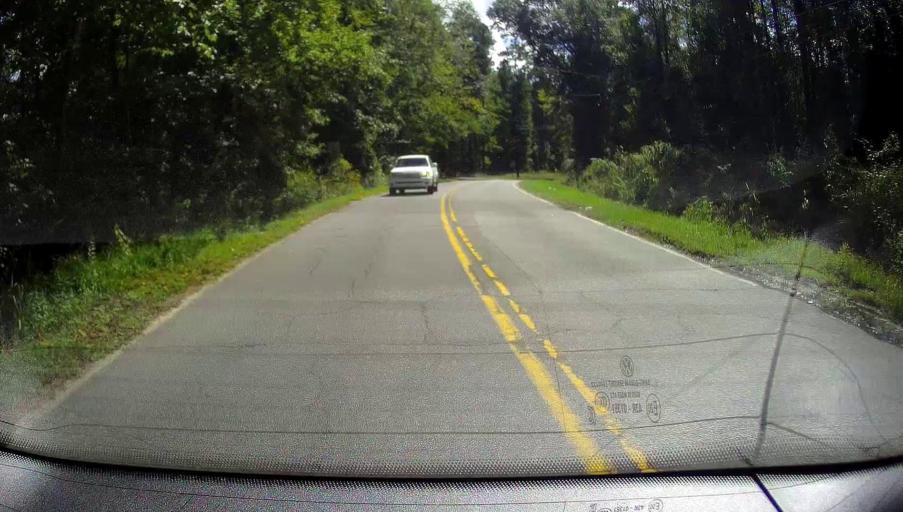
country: US
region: Georgia
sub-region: Bibb County
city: Macon
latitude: 32.8483
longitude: -83.5794
